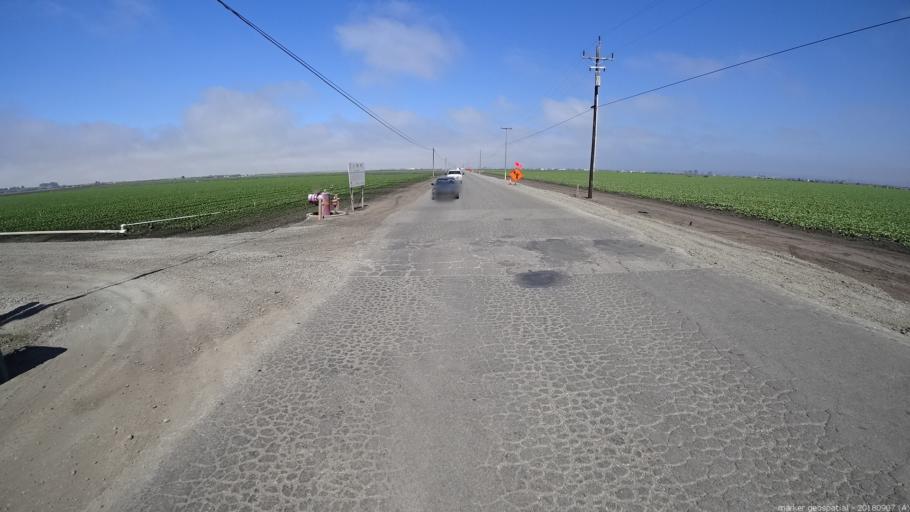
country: US
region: California
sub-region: Monterey County
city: Castroville
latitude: 36.7120
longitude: -121.7394
